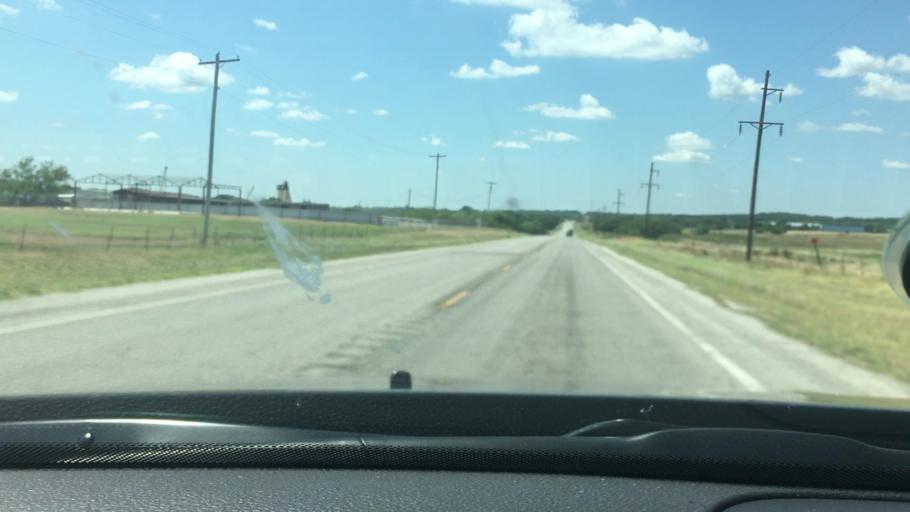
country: US
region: Oklahoma
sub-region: Carter County
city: Ardmore
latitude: 34.0841
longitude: -97.1429
